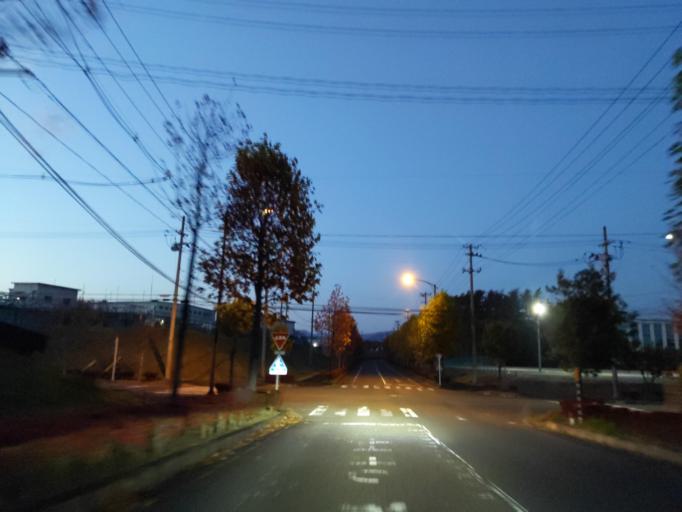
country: JP
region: Fukushima
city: Koriyama
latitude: 37.4421
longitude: 140.3063
